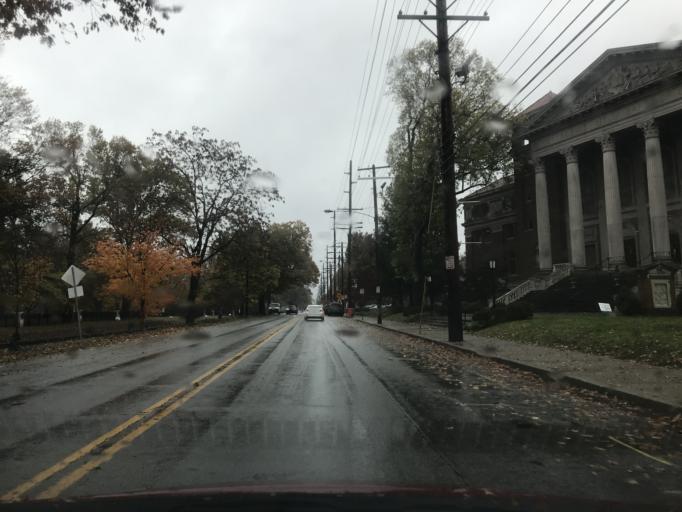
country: US
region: Kentucky
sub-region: Jefferson County
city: Indian Hills
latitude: 38.2547
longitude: -85.6905
